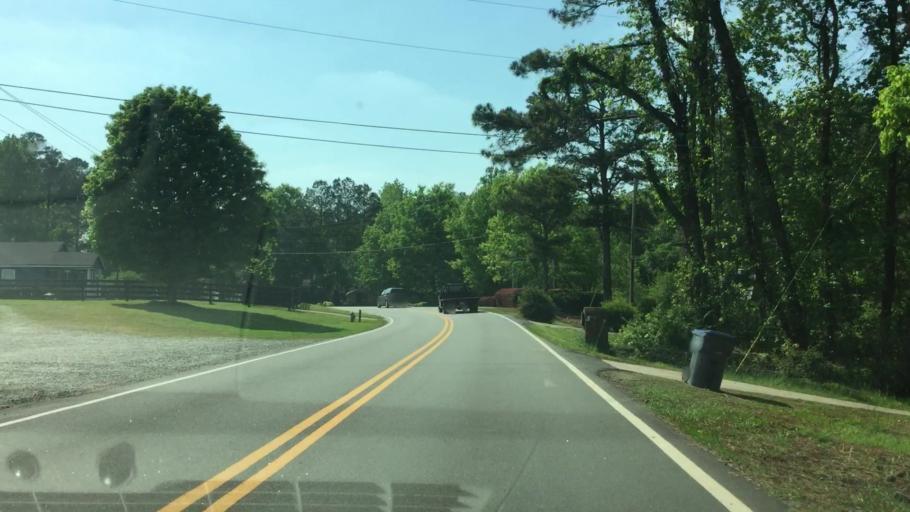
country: US
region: Georgia
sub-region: Fulton County
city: Milton
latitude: 34.1546
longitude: -84.2545
